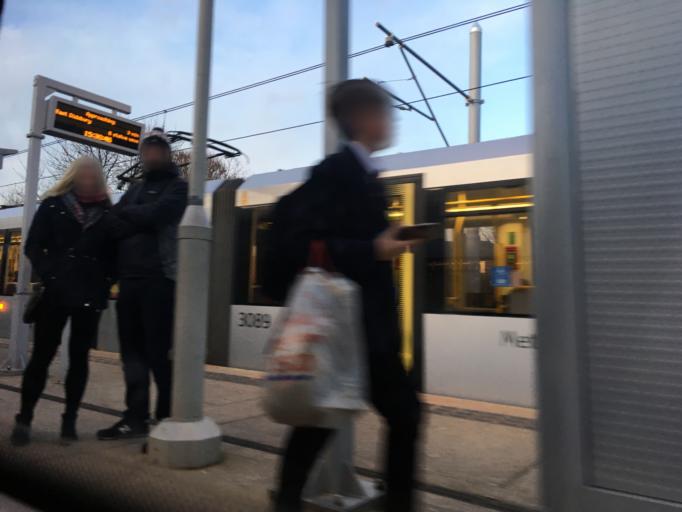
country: GB
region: England
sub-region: Manchester
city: Chorlton cum Hardy
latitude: 53.4388
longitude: -2.2656
